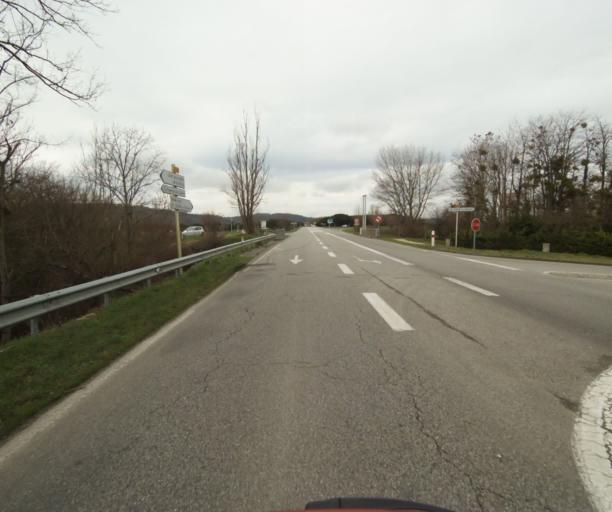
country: FR
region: Midi-Pyrenees
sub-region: Departement de l'Ariege
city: La Tour-du-Crieu
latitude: 43.1013
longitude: 1.6372
